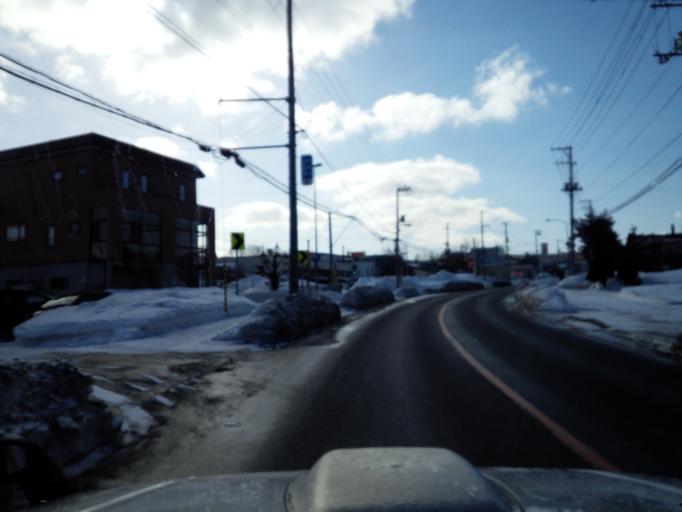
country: JP
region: Hokkaido
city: Sapporo
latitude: 42.9512
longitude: 141.3464
